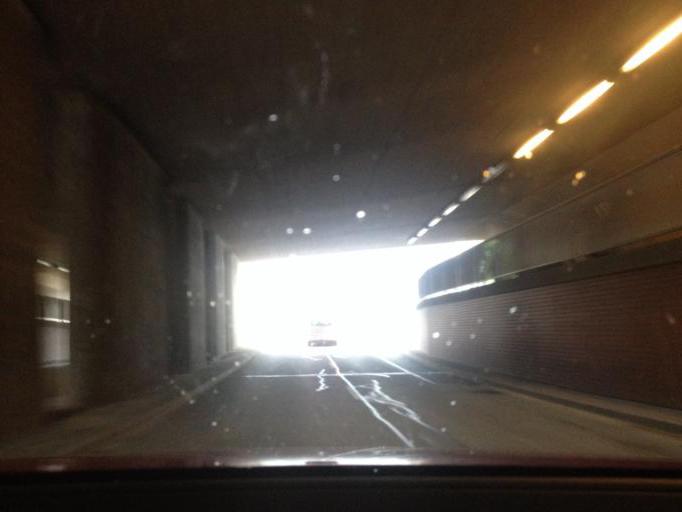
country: DE
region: Bavaria
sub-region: Regierungsbezirk Mittelfranken
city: Nuernberg
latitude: 49.4369
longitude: 11.1174
